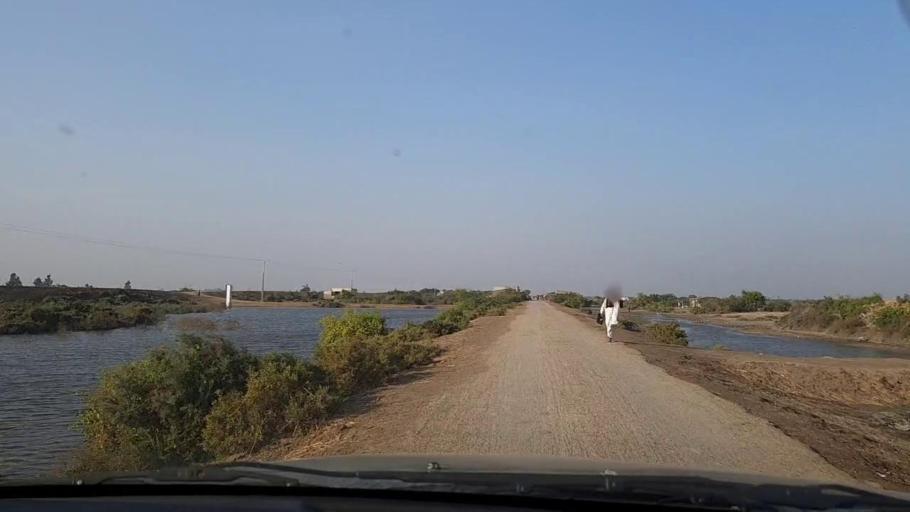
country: PK
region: Sindh
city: Chuhar Jamali
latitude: 24.3006
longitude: 67.7556
